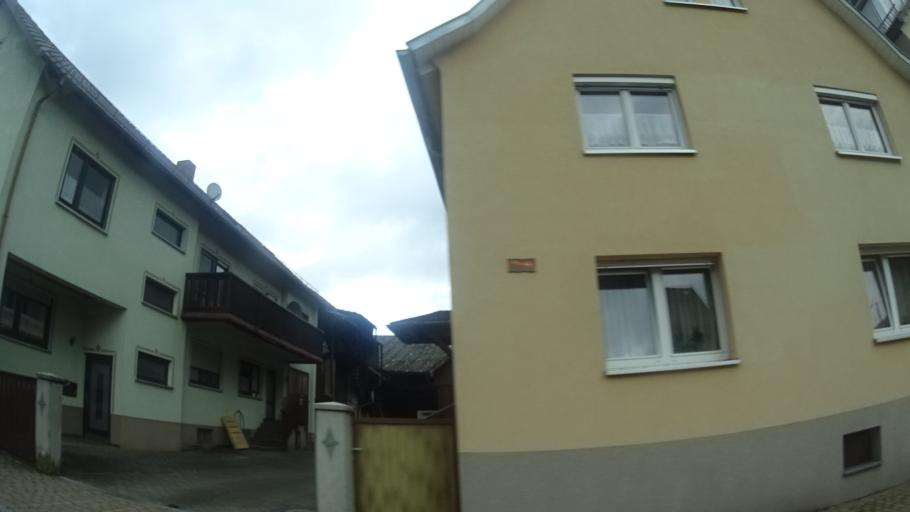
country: DE
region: Bavaria
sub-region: Regierungsbezirk Unterfranken
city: Oberelsbach
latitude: 50.3810
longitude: 10.1038
